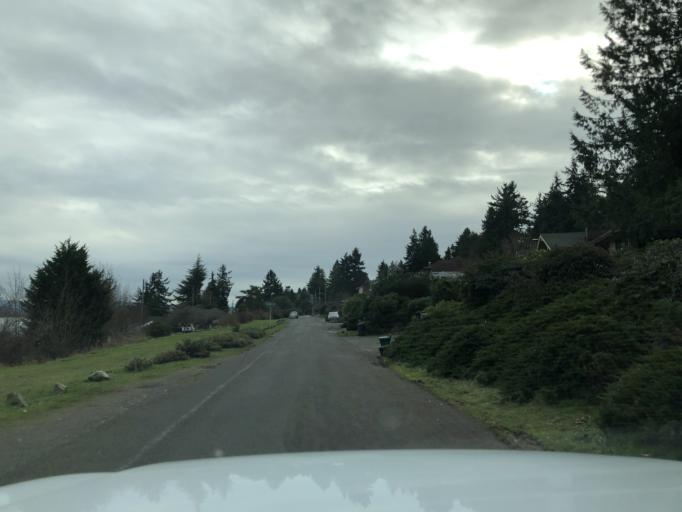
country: US
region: Washington
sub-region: King County
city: Inglewood-Finn Hill
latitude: 47.7036
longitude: -122.2749
